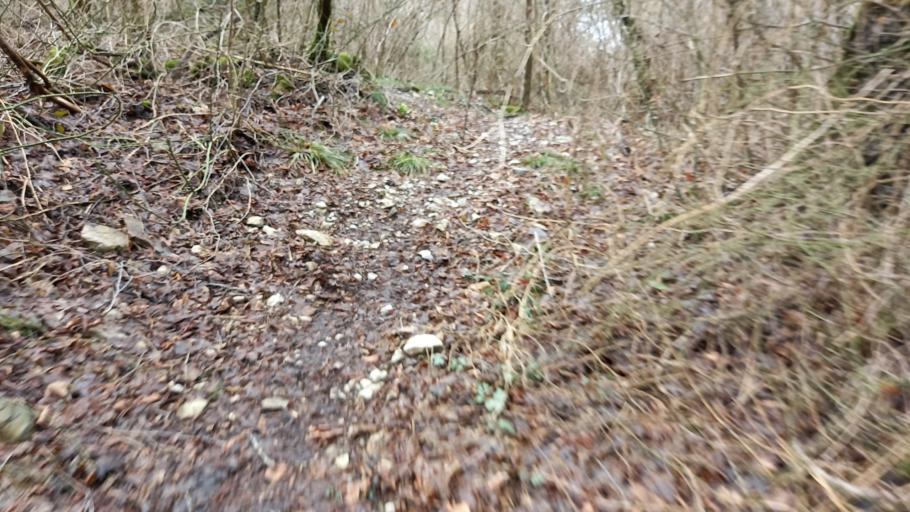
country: RU
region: Krasnodarskiy
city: Dzhubga
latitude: 44.4060
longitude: 38.7130
